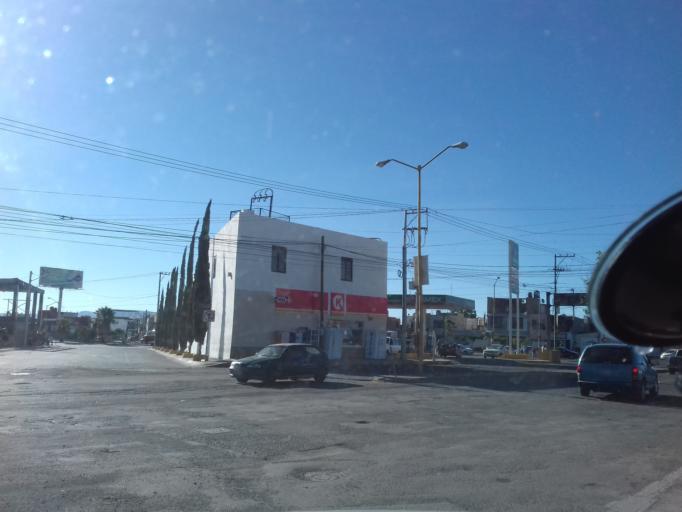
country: MX
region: Aguascalientes
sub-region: Aguascalientes
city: San Sebastian [Fraccionamiento]
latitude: 21.8514
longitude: -102.2692
